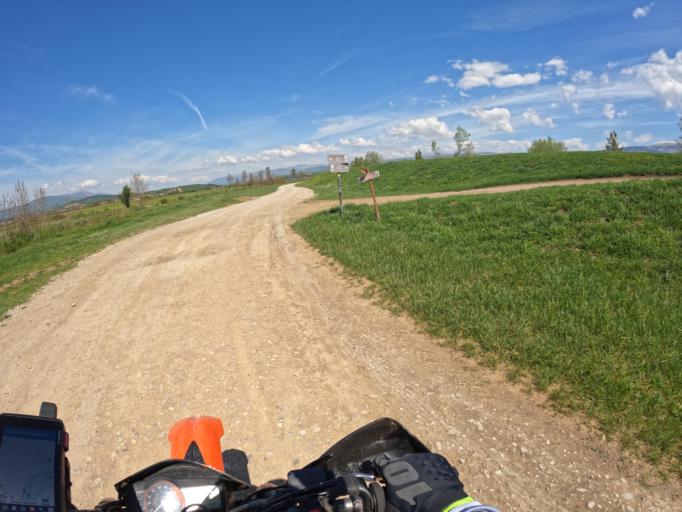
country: HR
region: Splitsko-Dalmatinska
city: Otok
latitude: 43.6906
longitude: 16.7128
